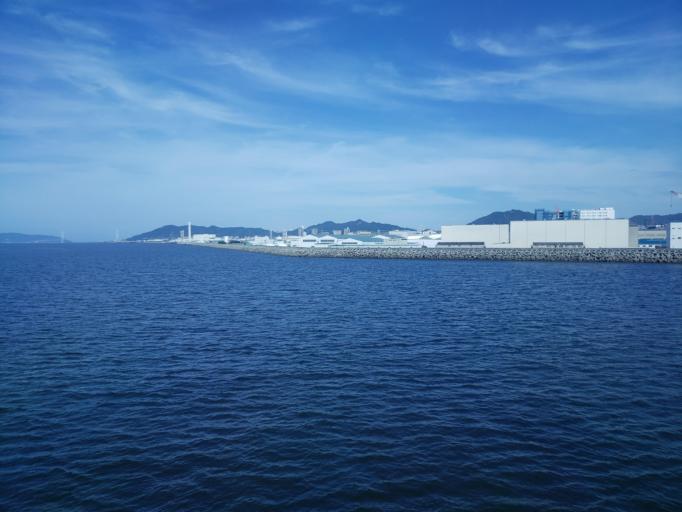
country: JP
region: Hyogo
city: Kobe
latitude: 34.6490
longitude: 135.1882
